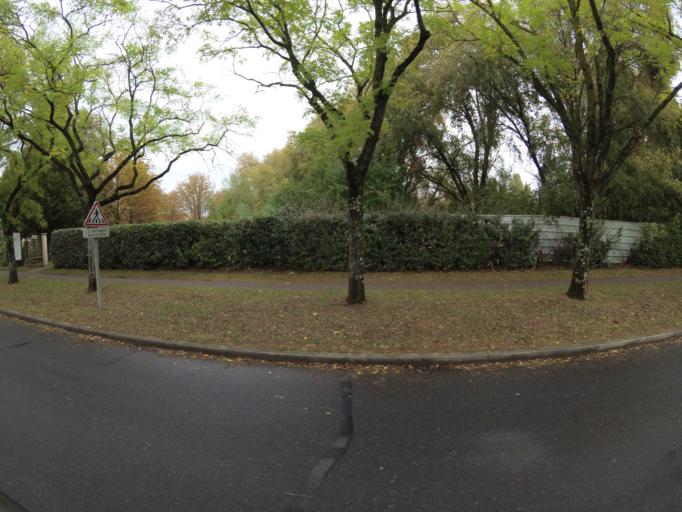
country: FR
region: Ile-de-France
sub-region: Departement de Seine-et-Marne
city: Guermantes
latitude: 48.8450
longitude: 2.7112
